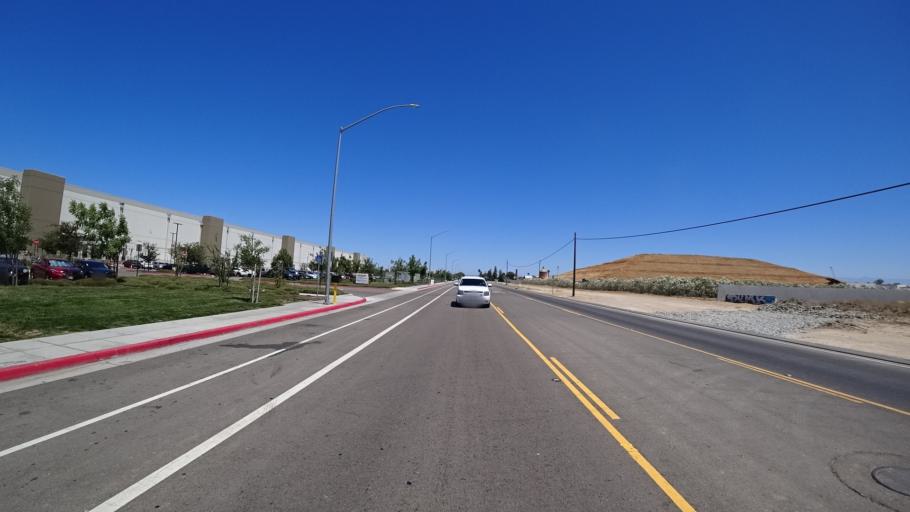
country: US
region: California
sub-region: Fresno County
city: Easton
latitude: 36.6831
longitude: -119.7637
